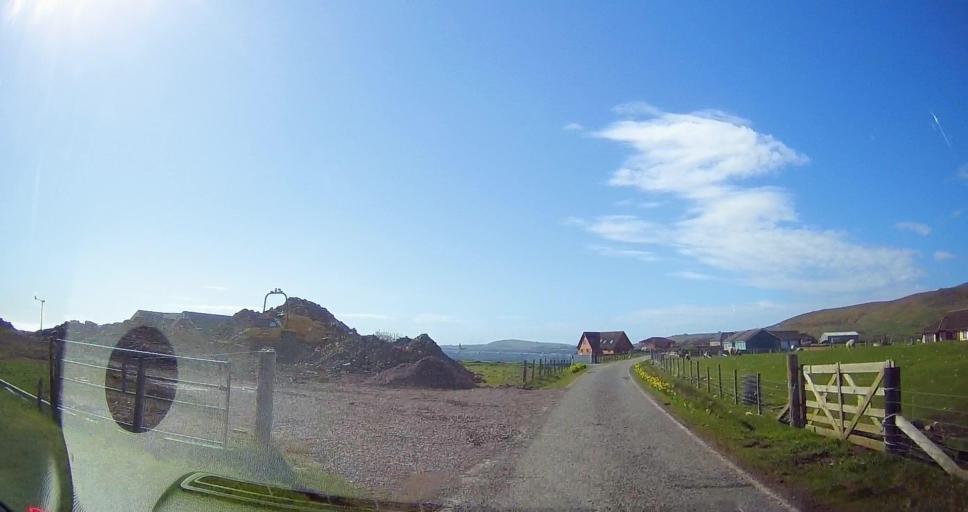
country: GB
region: Scotland
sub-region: Shetland Islands
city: Sandwick
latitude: 60.0382
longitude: -1.2178
